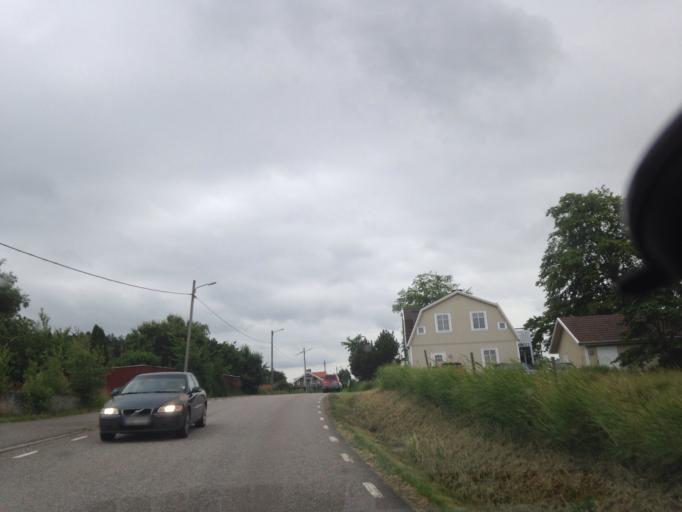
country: SE
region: Vaestra Goetaland
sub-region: Kungalvs Kommun
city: Kode
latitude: 57.8421
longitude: 11.7935
